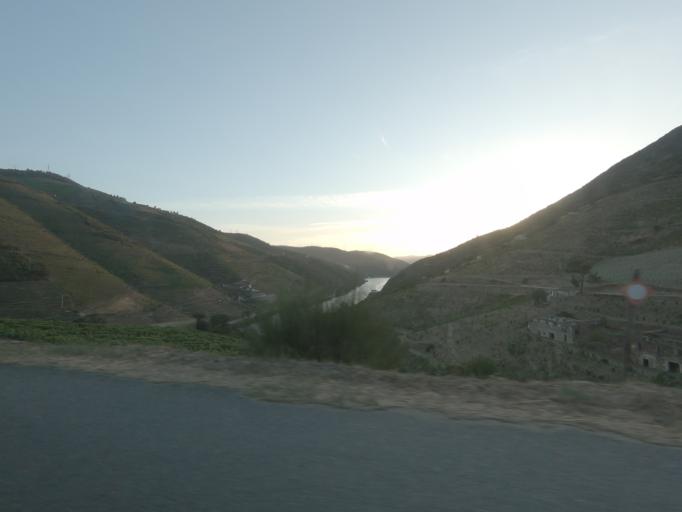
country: PT
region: Viseu
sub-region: Armamar
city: Armamar
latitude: 41.1453
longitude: -7.7016
